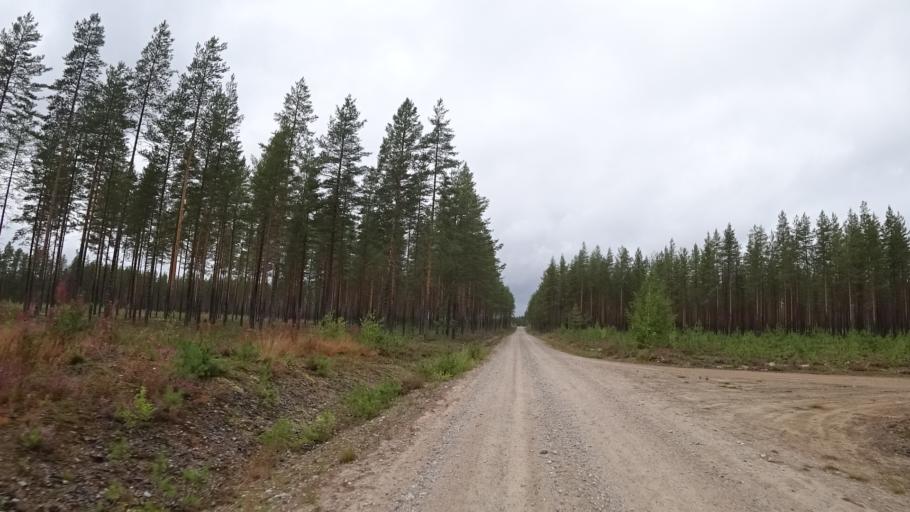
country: FI
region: North Karelia
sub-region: Pielisen Karjala
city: Lieksa
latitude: 63.5272
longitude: 30.0806
